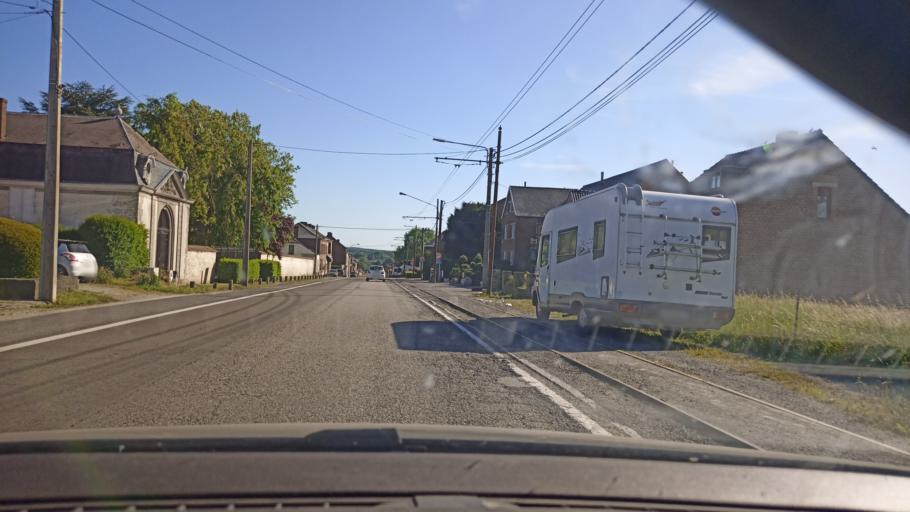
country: BE
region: Wallonia
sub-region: Province du Hainaut
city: Lobbes
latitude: 50.3551
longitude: 4.2687
